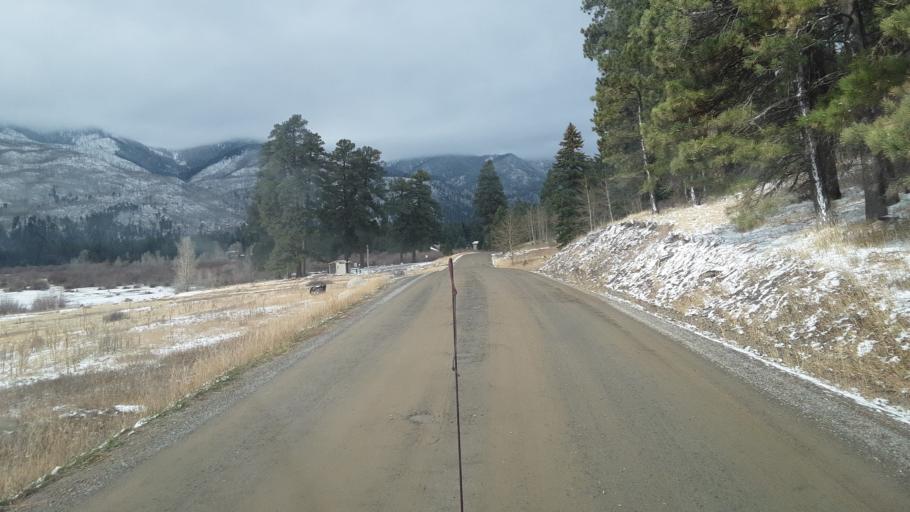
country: US
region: Colorado
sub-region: La Plata County
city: Bayfield
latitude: 37.4312
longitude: -107.5413
